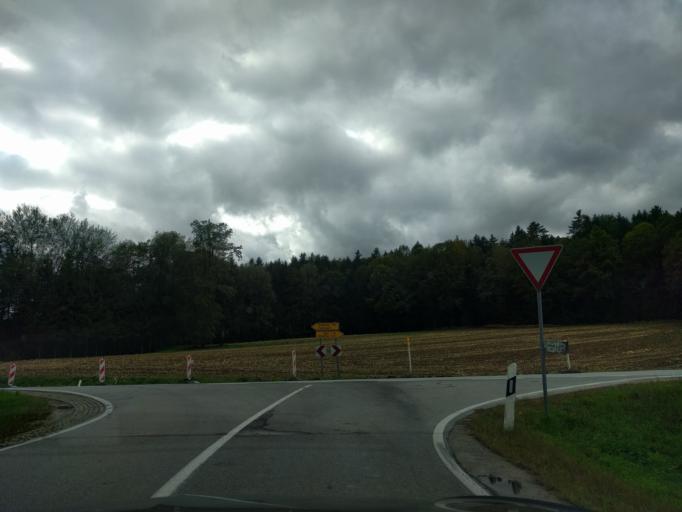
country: DE
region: Bavaria
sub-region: Lower Bavaria
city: Auerbach
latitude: 48.8281
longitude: 13.0912
